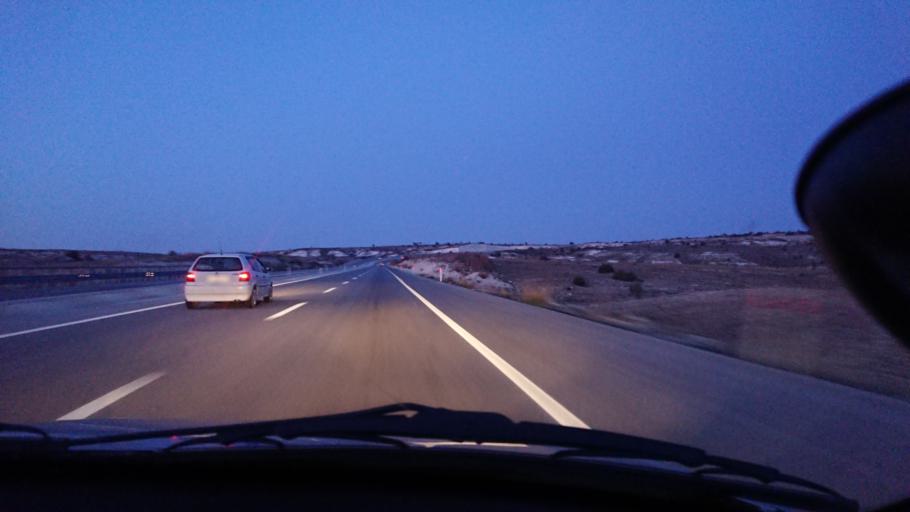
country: TR
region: Kuetahya
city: Cavdarhisar
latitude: 39.1358
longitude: 29.5568
